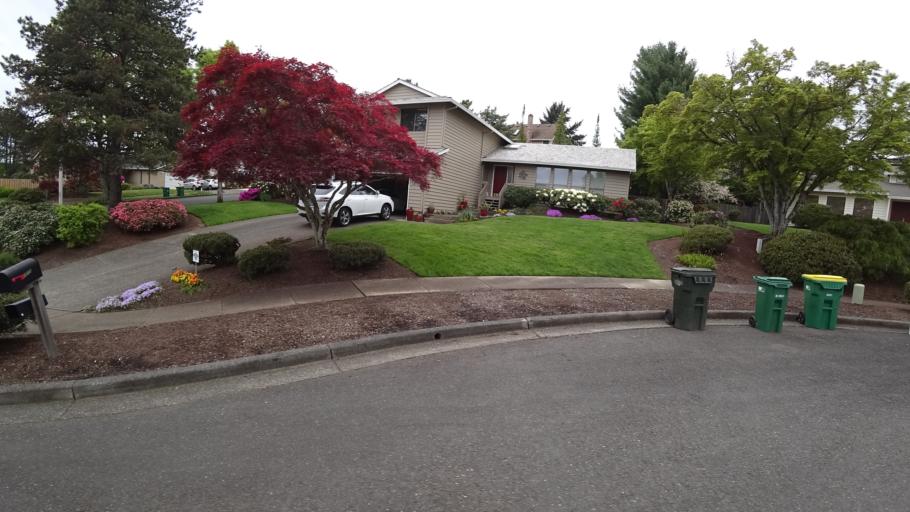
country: US
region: Oregon
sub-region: Washington County
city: Beaverton
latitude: 45.4563
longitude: -122.8220
